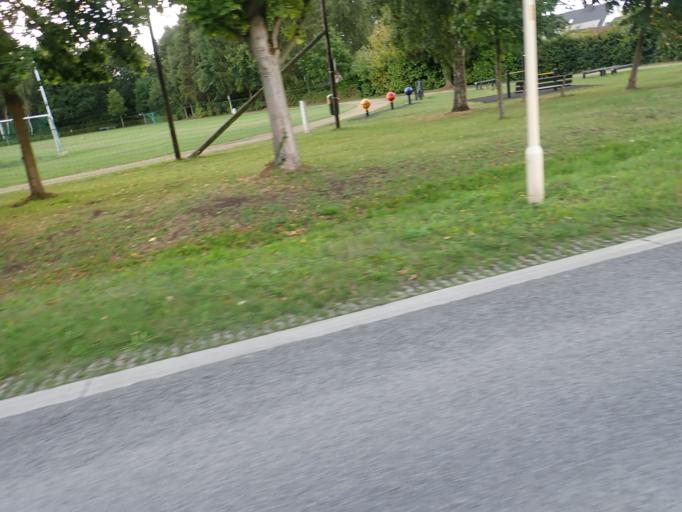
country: BE
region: Flanders
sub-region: Provincie Antwerpen
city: Zandhoven
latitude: 51.2425
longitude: 4.6504
